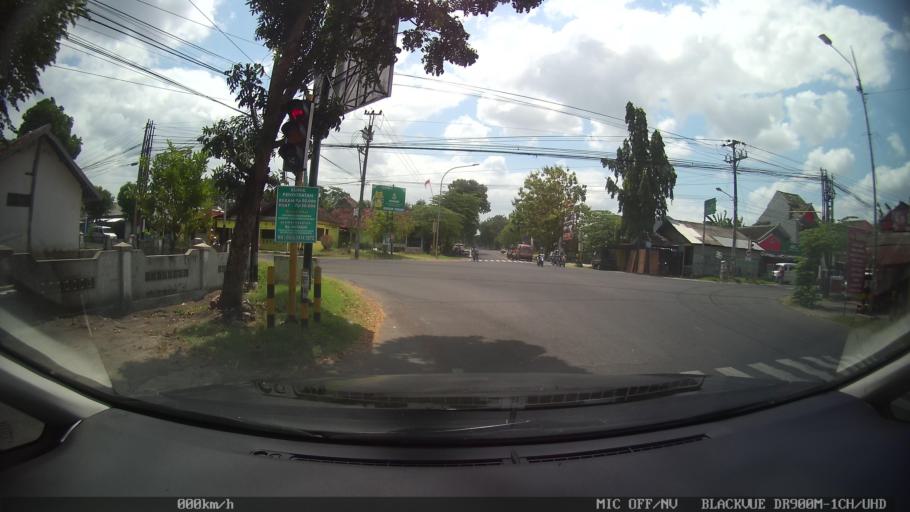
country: ID
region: Daerah Istimewa Yogyakarta
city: Bantul
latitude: -7.8951
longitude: 110.3466
